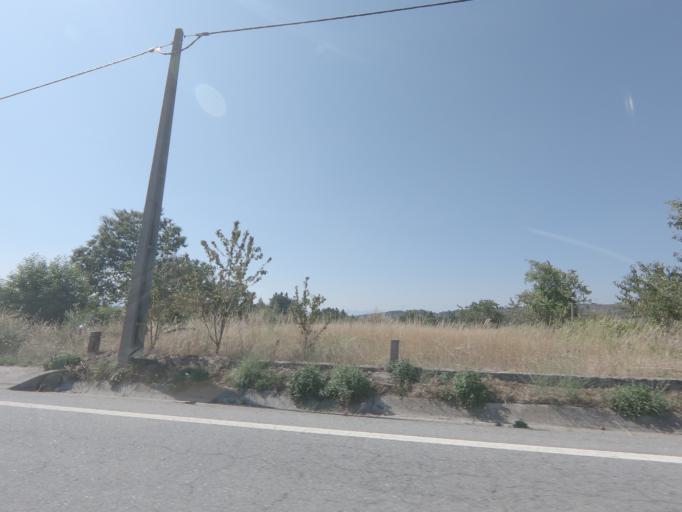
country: PT
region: Viseu
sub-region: Moimenta da Beira
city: Moimenta da Beira
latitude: 41.0094
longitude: -7.6789
